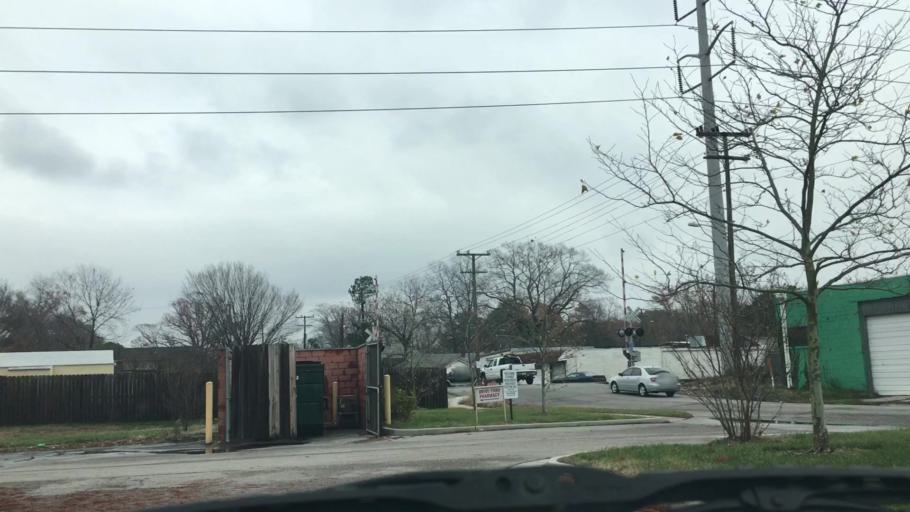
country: US
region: Virginia
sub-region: City of Norfolk
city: Norfolk
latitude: 36.8752
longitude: -76.2515
